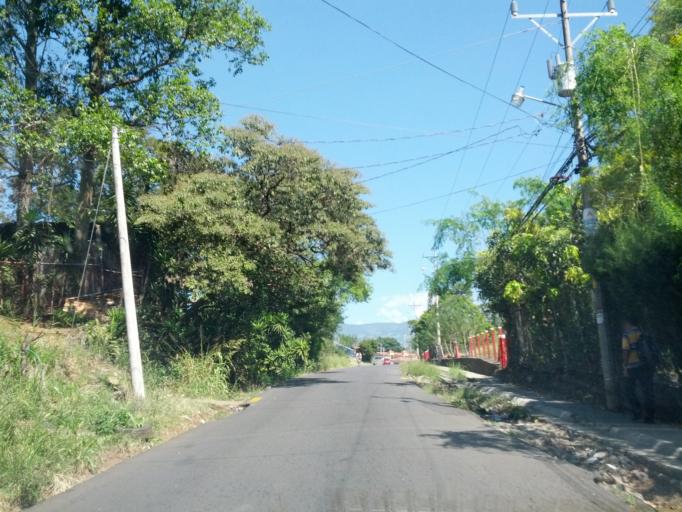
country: CR
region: Heredia
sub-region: Canton de Belen
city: San Antonio
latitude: 10.0071
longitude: -84.1870
